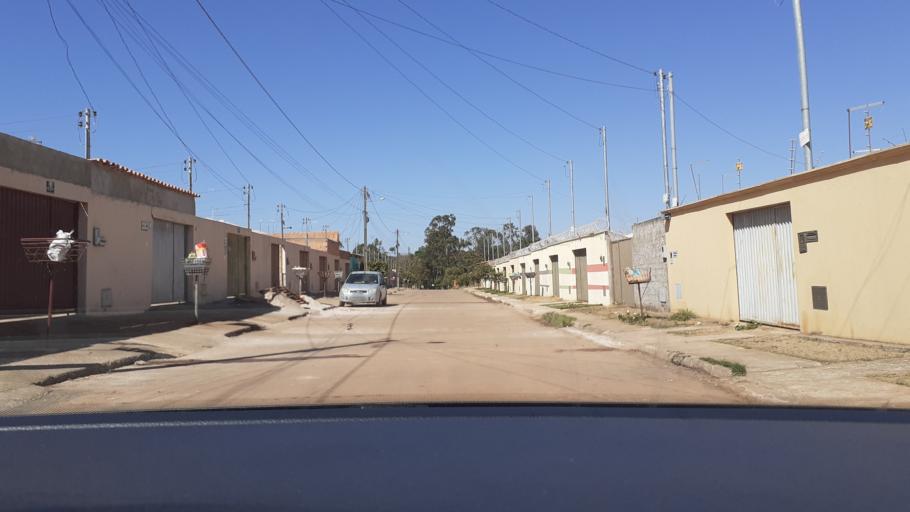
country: BR
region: Goias
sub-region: Aparecida De Goiania
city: Aparecida de Goiania
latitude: -16.8784
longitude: -49.2611
